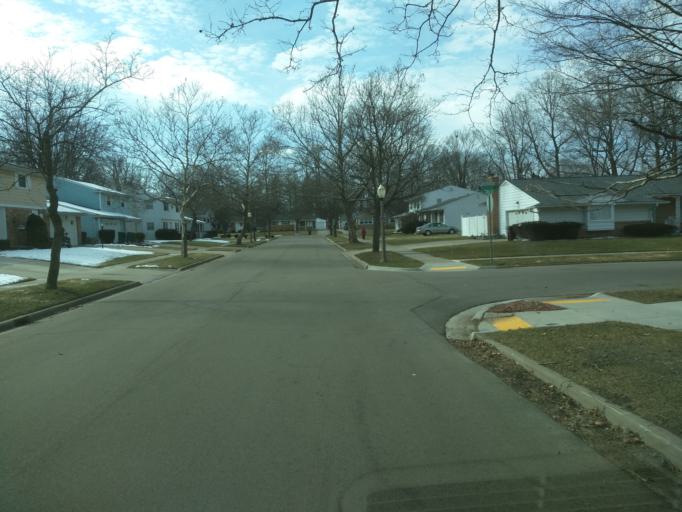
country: US
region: Michigan
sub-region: Ingham County
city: Edgemont Park
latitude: 42.7053
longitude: -84.5904
